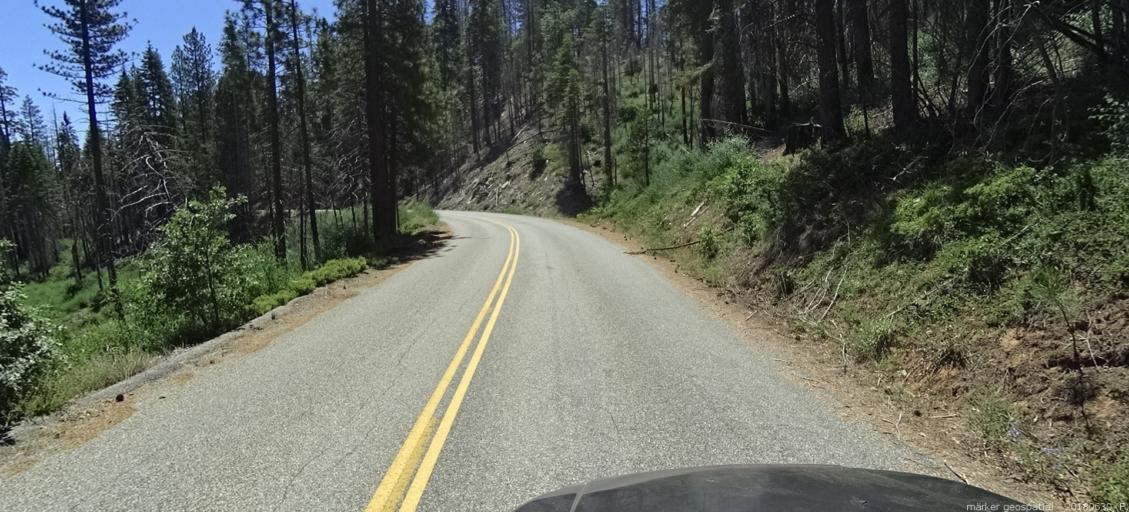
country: US
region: California
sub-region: Fresno County
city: Auberry
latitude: 37.3230
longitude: -119.3701
